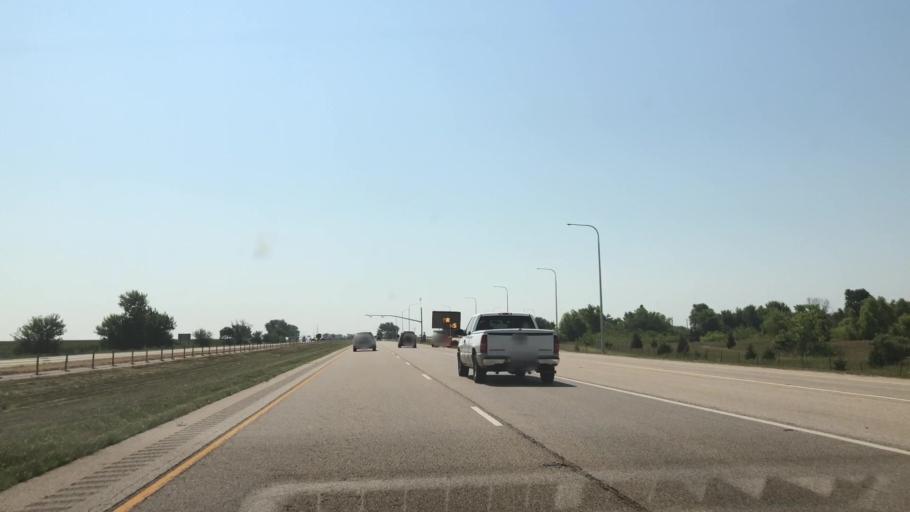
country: US
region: Illinois
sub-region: McLean County
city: Danvers
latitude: 40.5603
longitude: -89.1107
